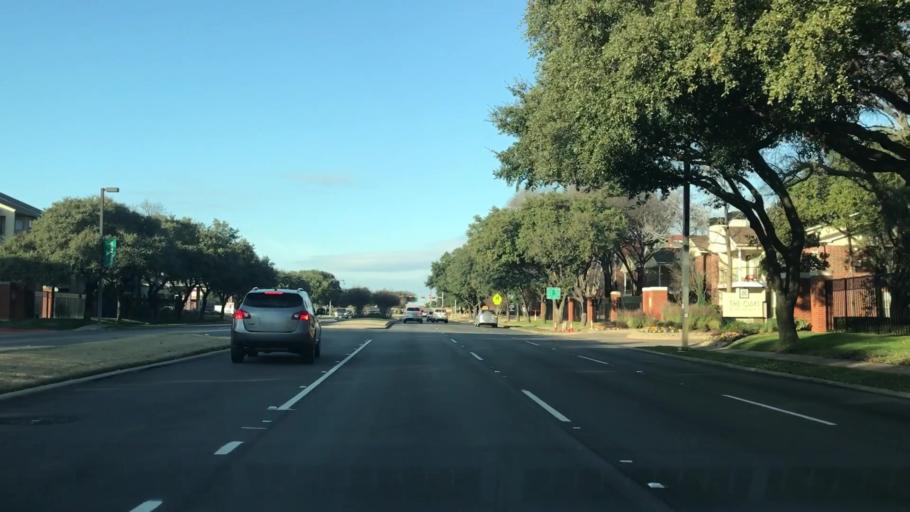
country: US
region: Texas
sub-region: Dallas County
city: Farmers Branch
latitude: 32.9384
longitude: -96.9520
